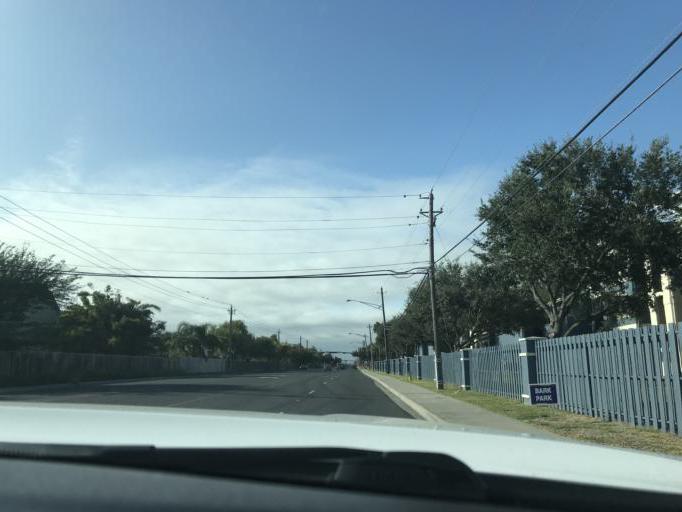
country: US
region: Texas
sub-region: Nueces County
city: Corpus Christi
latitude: 27.6771
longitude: -97.3705
